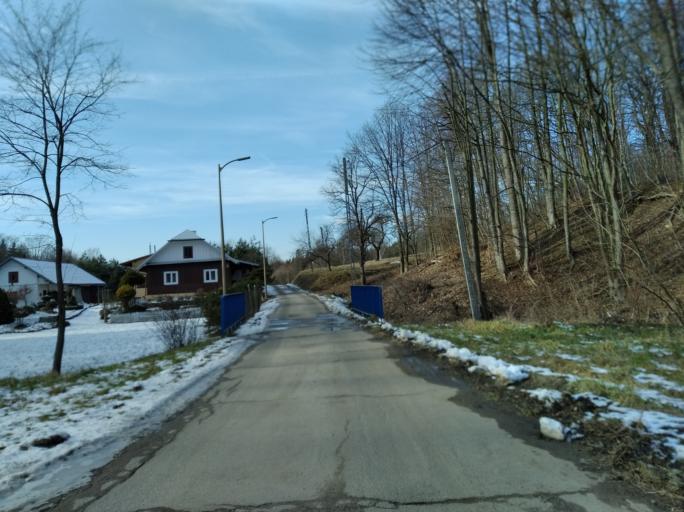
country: PL
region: Subcarpathian Voivodeship
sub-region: Powiat krosnienski
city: Korczyna
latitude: 49.7684
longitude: 21.7985
